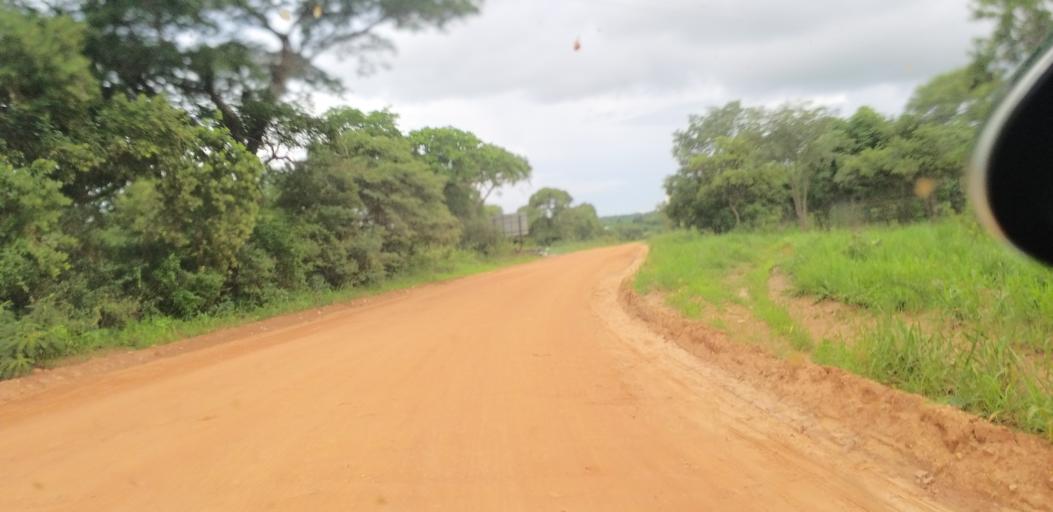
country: ZM
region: Lusaka
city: Lusaka
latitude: -15.1984
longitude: 28.4406
